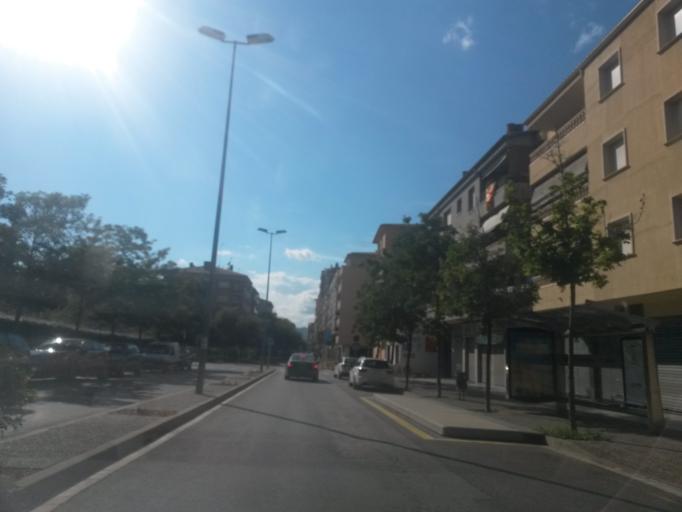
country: ES
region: Catalonia
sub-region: Provincia de Girona
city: Girona
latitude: 41.9689
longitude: 2.8193
